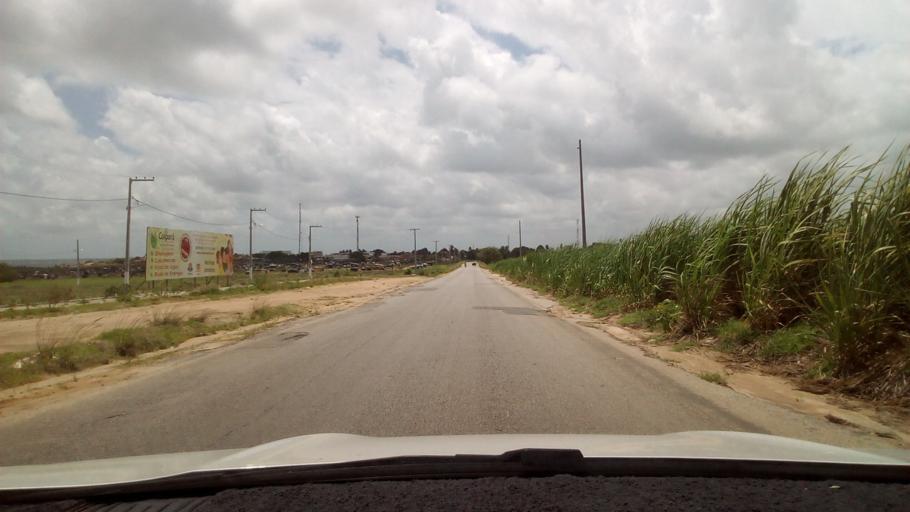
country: BR
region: Paraiba
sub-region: Caapora
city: Caapora
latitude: -7.5050
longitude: -34.9176
